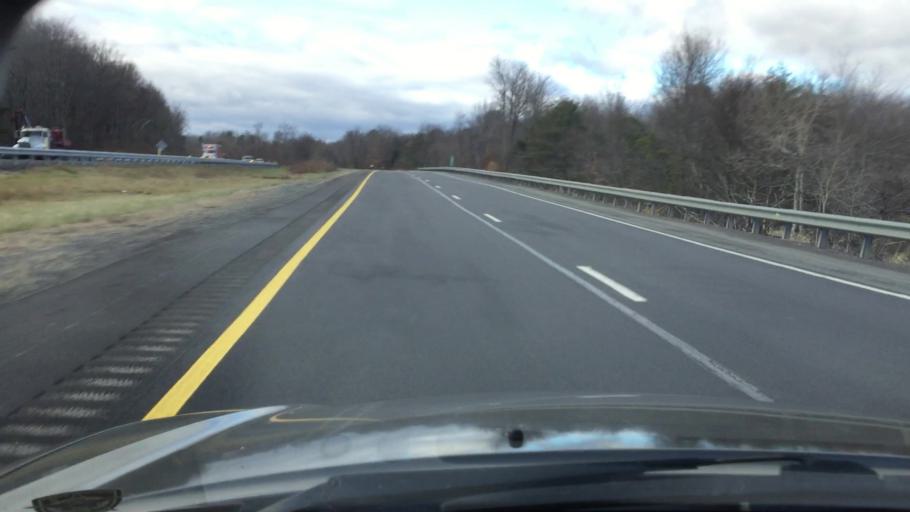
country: US
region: Pennsylvania
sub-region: Monroe County
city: Pocono Pines
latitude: 41.0769
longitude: -75.5064
